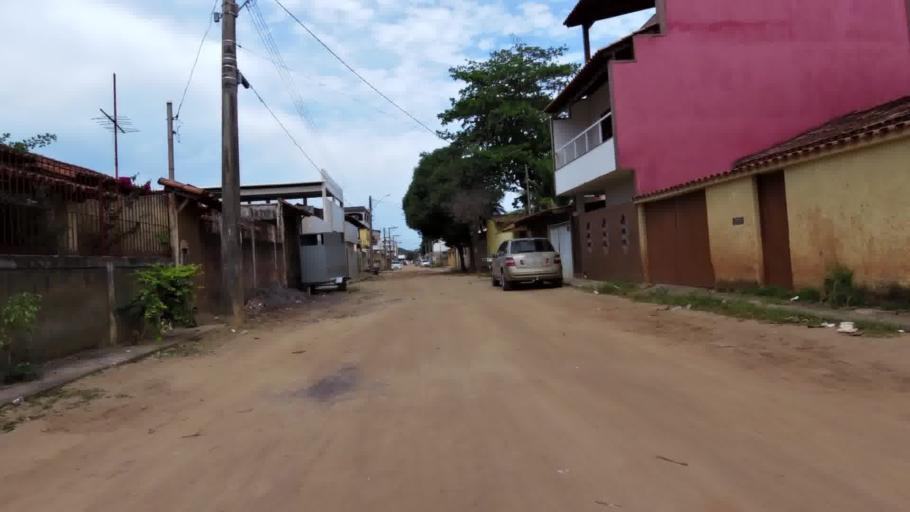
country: BR
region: Espirito Santo
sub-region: Piuma
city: Piuma
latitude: -20.8401
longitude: -40.7350
